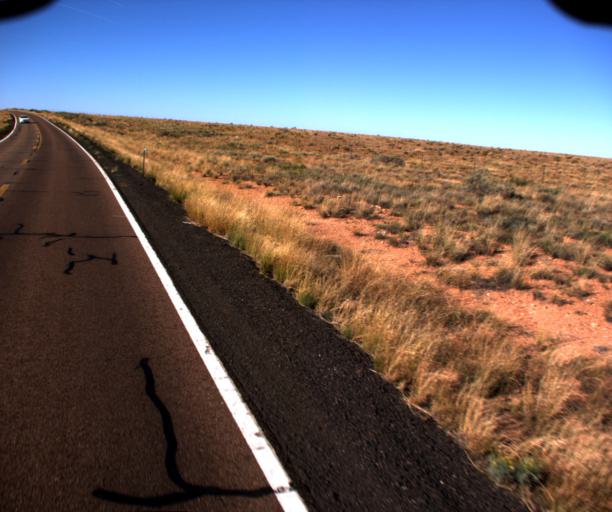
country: US
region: Arizona
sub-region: Navajo County
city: Holbrook
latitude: 34.7757
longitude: -110.2381
